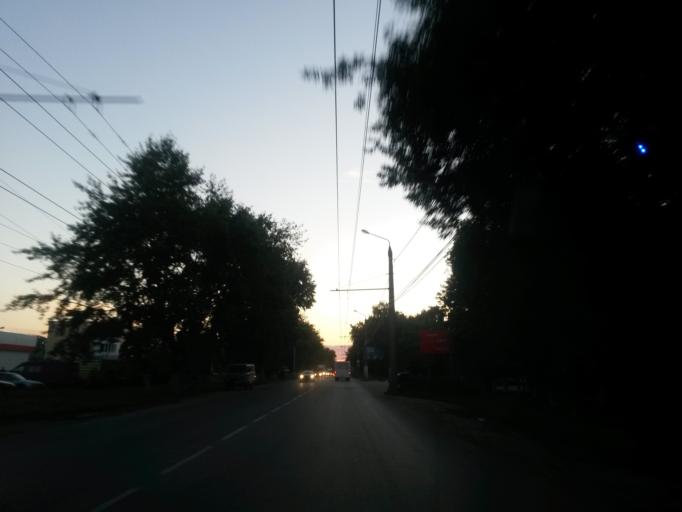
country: RU
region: Ivanovo
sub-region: Gorod Ivanovo
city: Ivanovo
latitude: 56.9979
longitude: 40.9544
